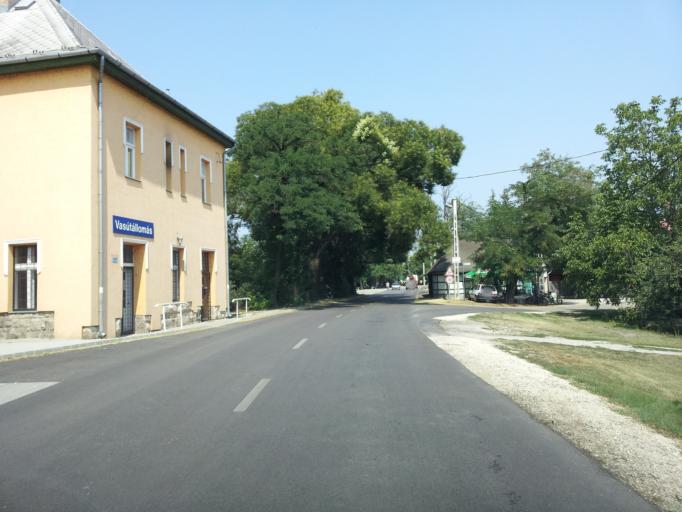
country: HU
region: Pest
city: Dunavarsany
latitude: 47.2743
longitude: 19.0653
